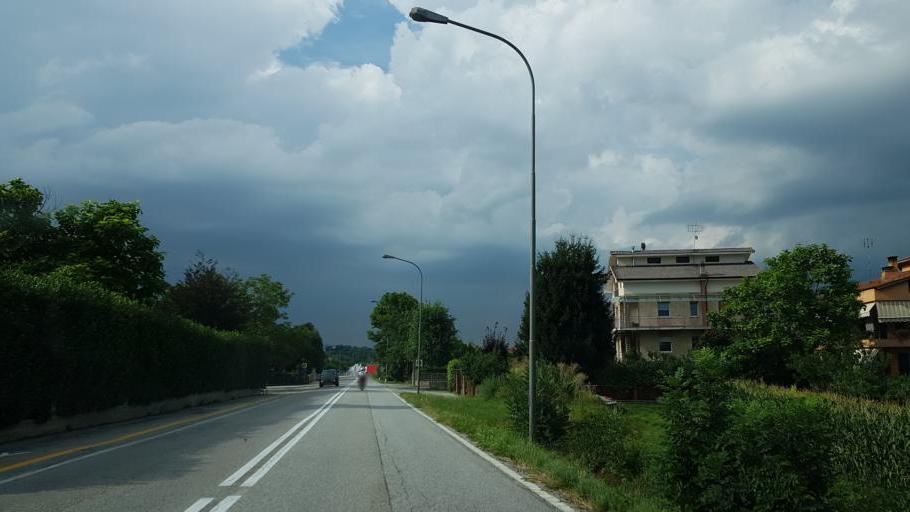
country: IT
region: Piedmont
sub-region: Provincia di Cuneo
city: Vignolo
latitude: 44.3588
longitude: 7.4772
